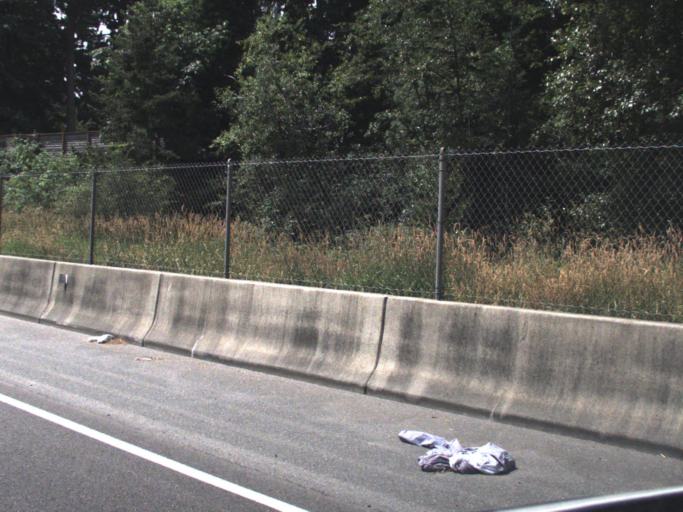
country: US
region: Washington
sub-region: King County
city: Seattle
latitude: 47.6433
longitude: -122.3139
